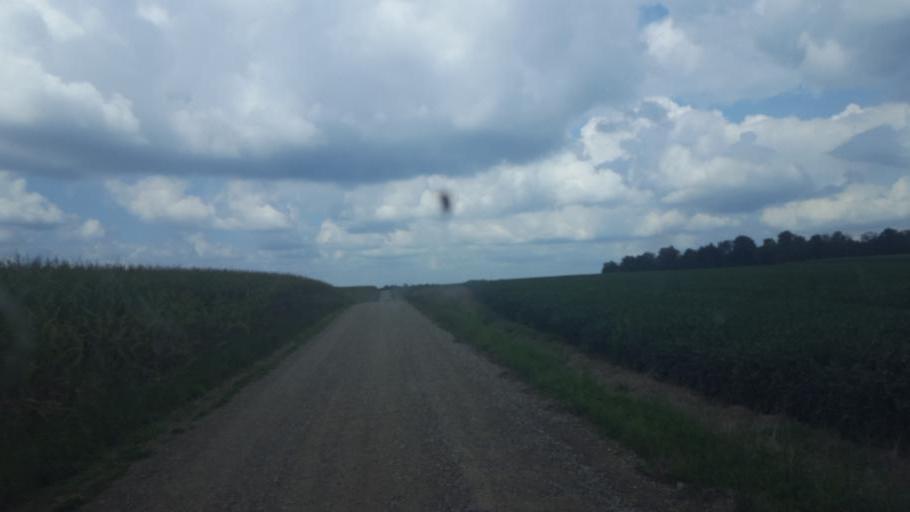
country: US
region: Ohio
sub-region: Knox County
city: Gambier
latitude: 40.3662
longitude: -82.3243
